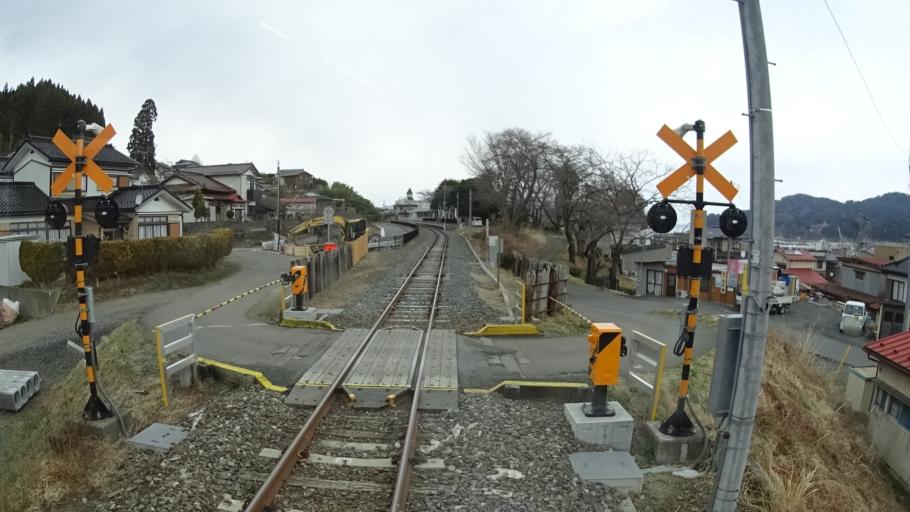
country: JP
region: Iwate
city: Otsuchi
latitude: 39.3692
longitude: 141.9382
